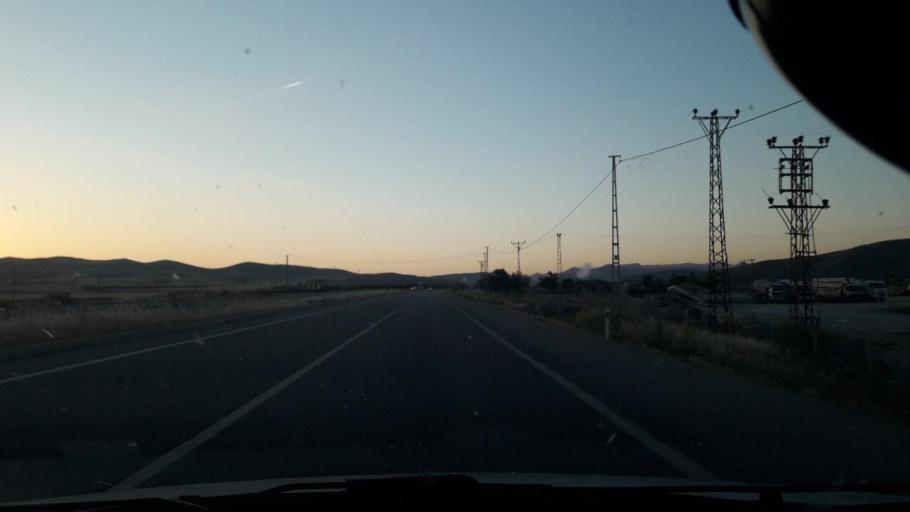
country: TR
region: Malatya
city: Yazihan
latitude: 38.6099
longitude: 38.1752
